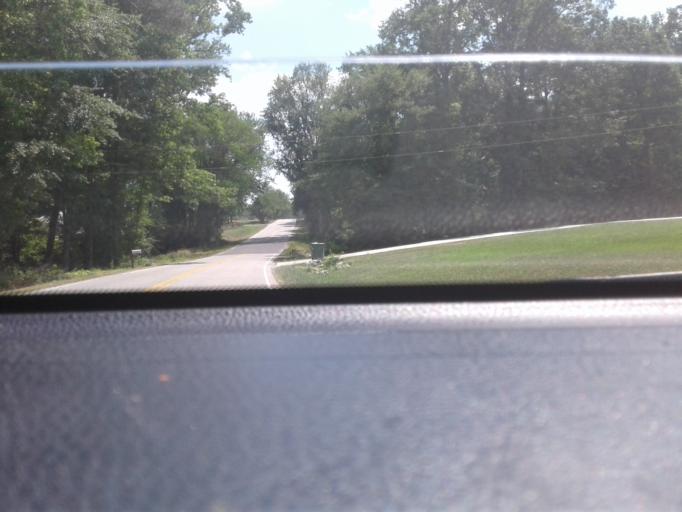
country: US
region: North Carolina
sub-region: Harnett County
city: Erwin
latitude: 35.2817
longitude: -78.6718
